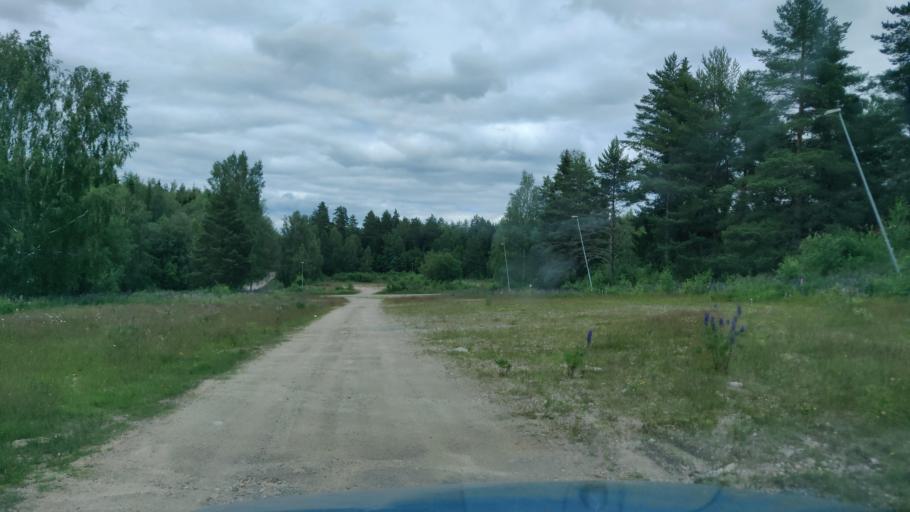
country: SE
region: Vaermland
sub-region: Hagfors Kommun
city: Hagfors
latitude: 60.0301
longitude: 13.7123
